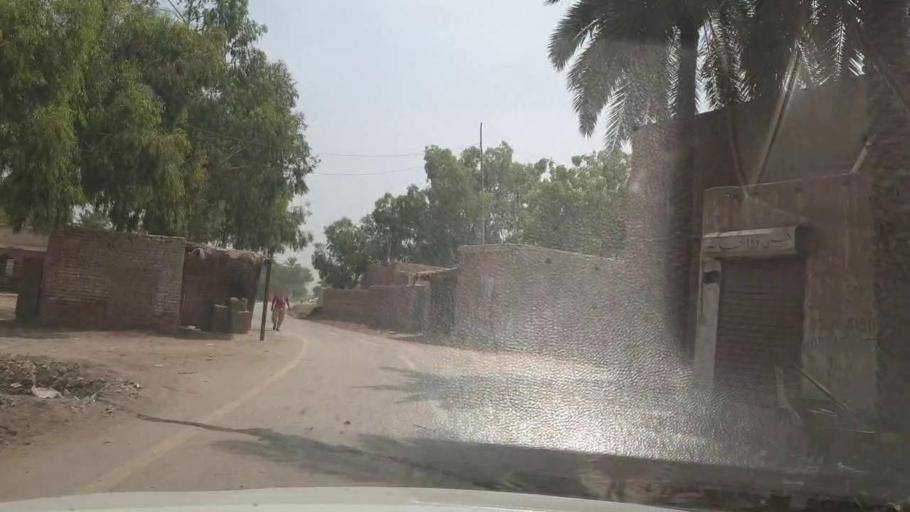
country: PK
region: Sindh
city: Kot Diji
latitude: 27.3710
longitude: 68.6480
